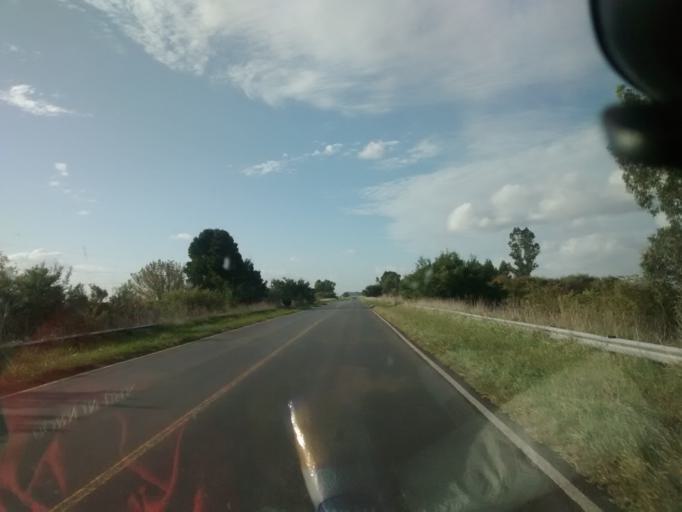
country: AR
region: Buenos Aires
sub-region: Partido de Ayacucho
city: Ayacucho
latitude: -36.7084
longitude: -58.5742
